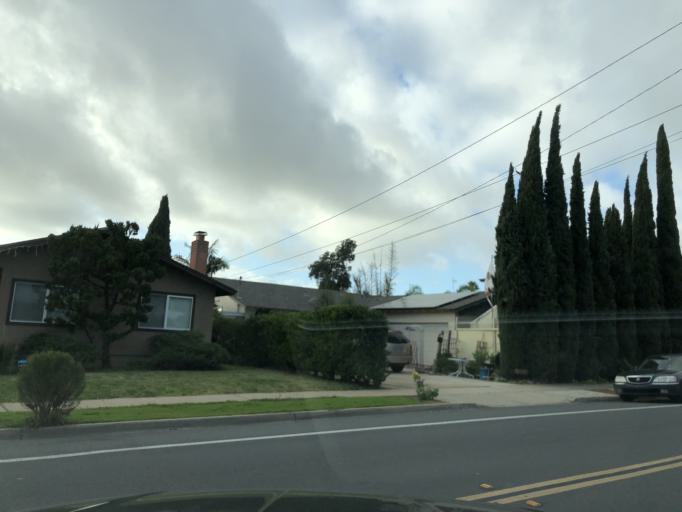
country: US
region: California
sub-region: San Diego County
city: La Jolla
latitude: 32.8133
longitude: -117.1817
